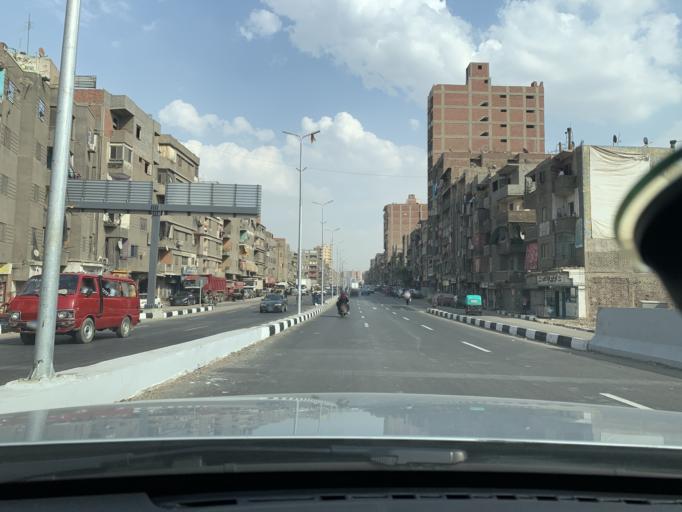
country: EG
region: Muhafazat al Qahirah
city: Cairo
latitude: 30.1248
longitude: 31.2990
